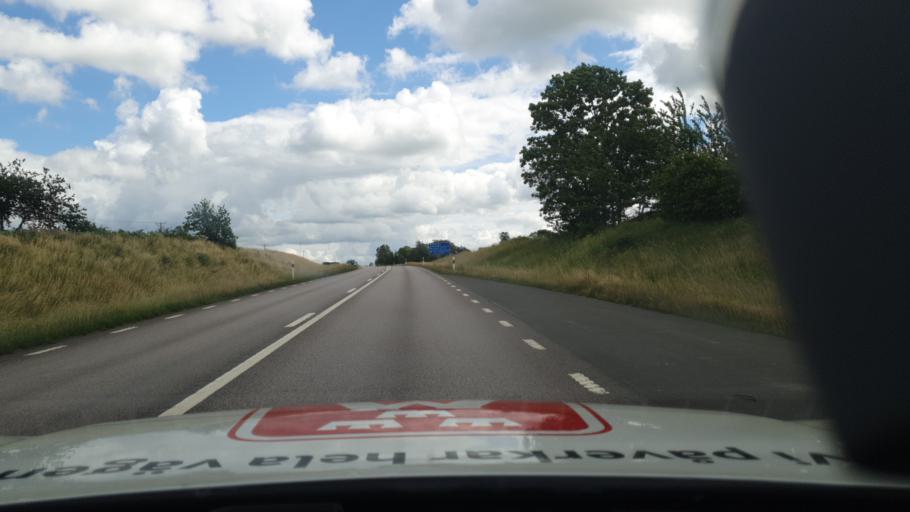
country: SE
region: Vaestra Goetaland
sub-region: Falkopings Kommun
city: Floby
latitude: 58.1684
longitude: 13.4118
